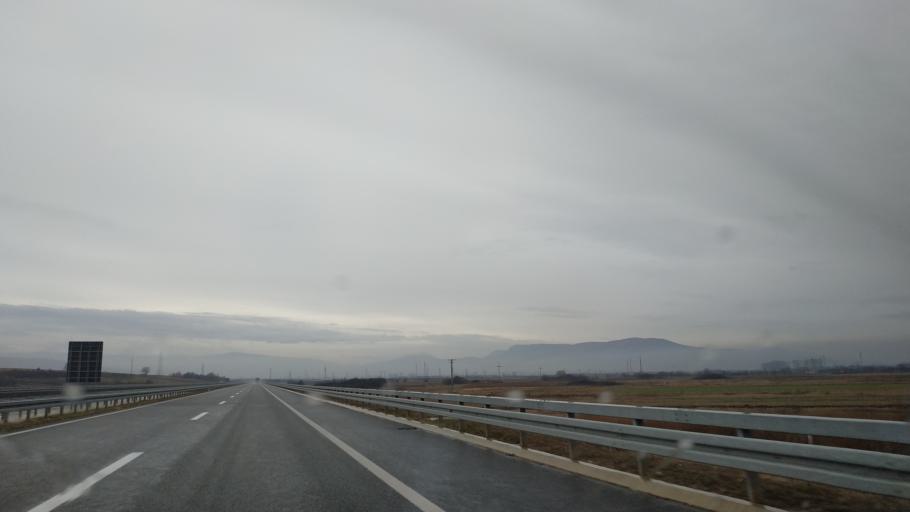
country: RS
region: Central Serbia
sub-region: Pirotski Okrug
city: Pirot
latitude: 43.1225
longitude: 22.6072
